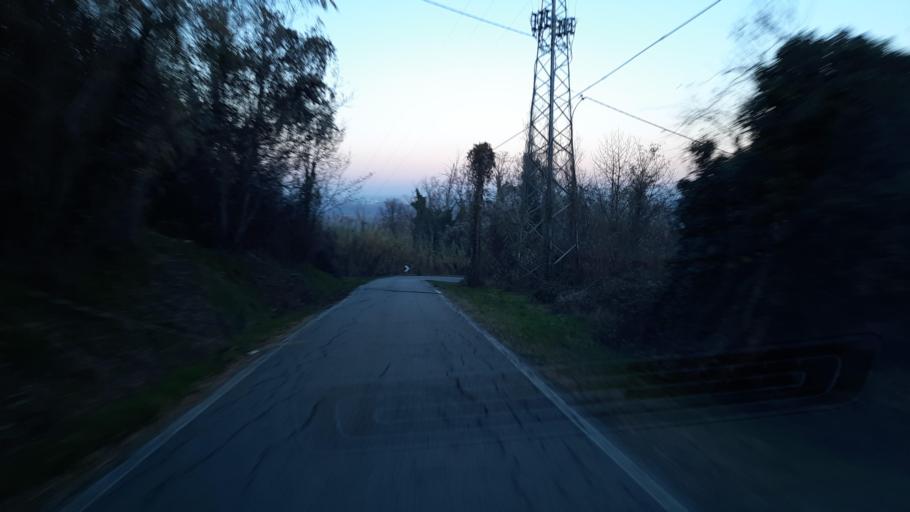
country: IT
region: Piedmont
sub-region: Provincia di Alessandria
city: Camino
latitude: 45.1733
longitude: 8.2770
